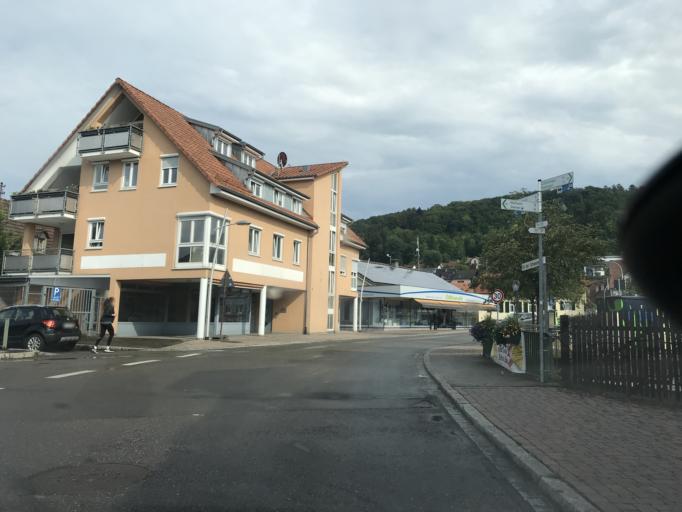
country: DE
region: Baden-Wuerttemberg
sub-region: Freiburg Region
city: Kandern
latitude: 47.7136
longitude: 7.6592
